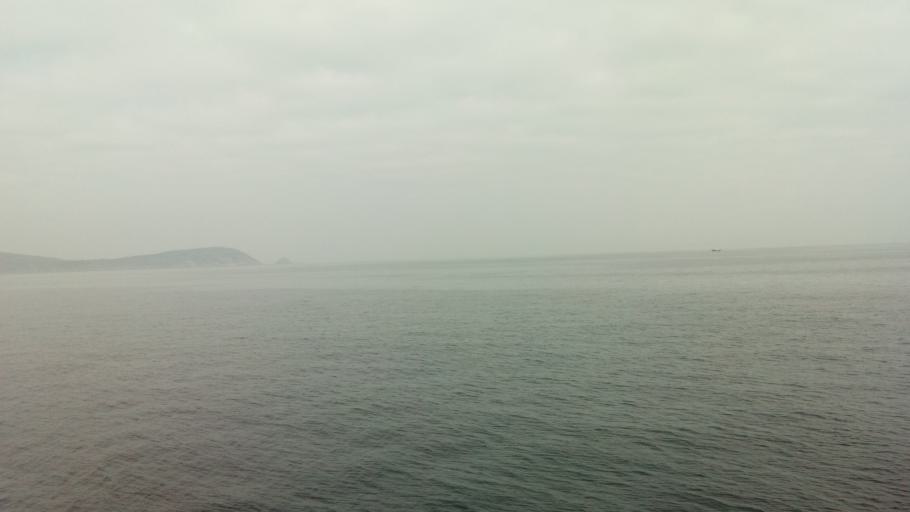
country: ES
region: Galicia
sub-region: Provincia de Pontevedra
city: Sanxenxo
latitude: 42.3796
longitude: -8.8853
